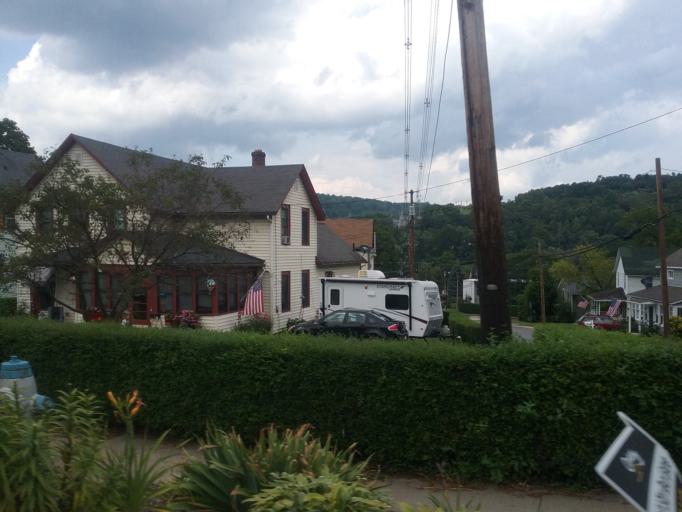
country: US
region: Pennsylvania
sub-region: Tioga County
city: Wellsboro
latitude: 41.7471
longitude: -77.2879
